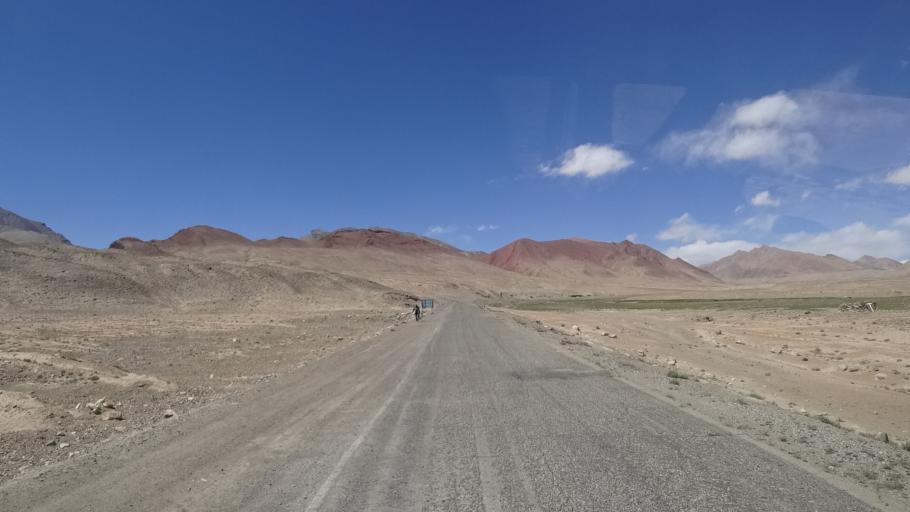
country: TJ
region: Gorno-Badakhshan
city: Murghob
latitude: 38.4937
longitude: 73.8497
